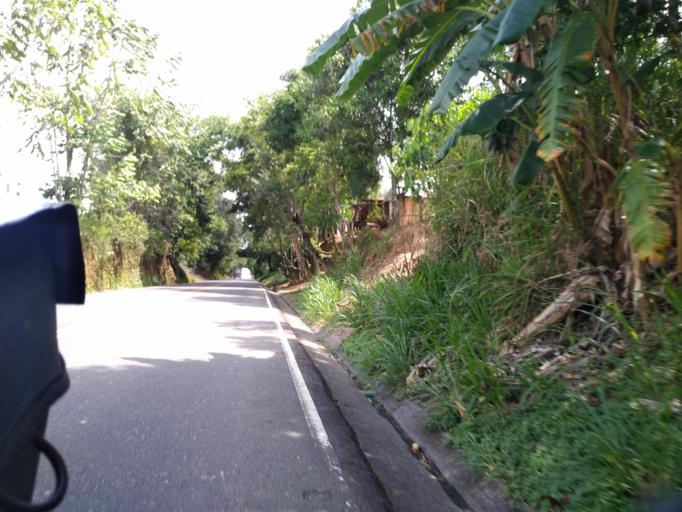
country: CO
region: Santander
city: Puerto Parra
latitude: 6.4868
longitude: -74.0403
